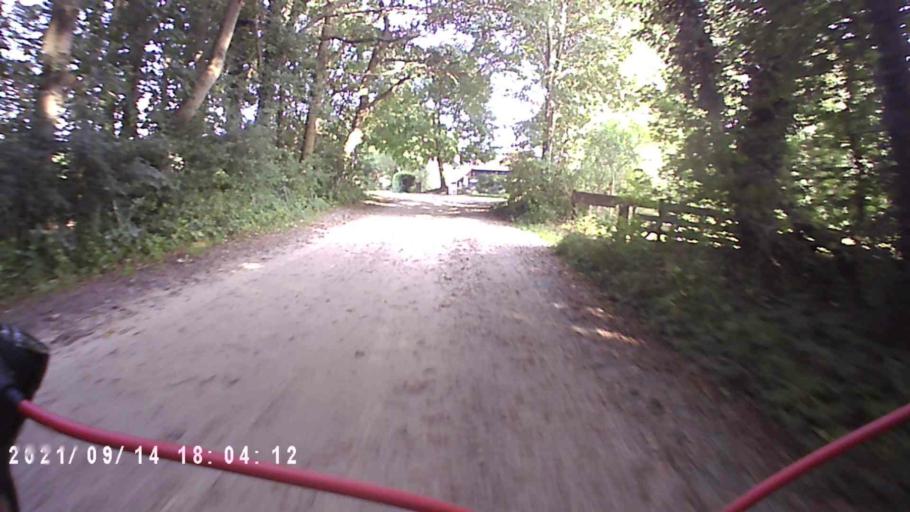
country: NL
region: Drenthe
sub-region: Gemeente Tynaarlo
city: Zuidlaren
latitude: 53.1114
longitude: 6.6540
